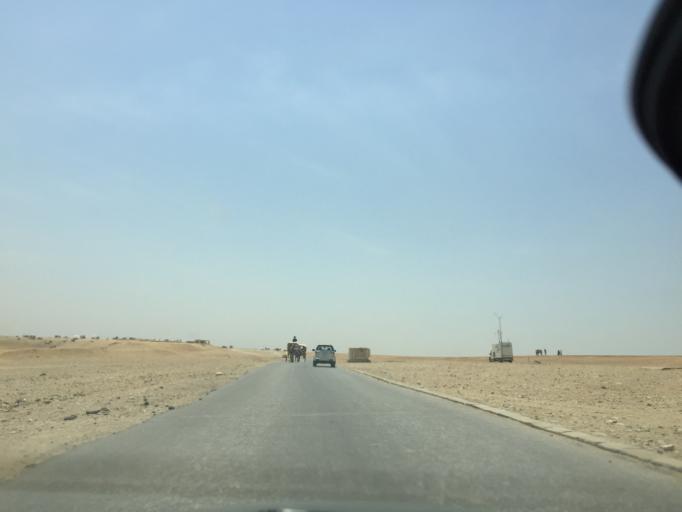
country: EG
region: Al Jizah
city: Al Jizah
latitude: 29.9734
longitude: 31.1250
